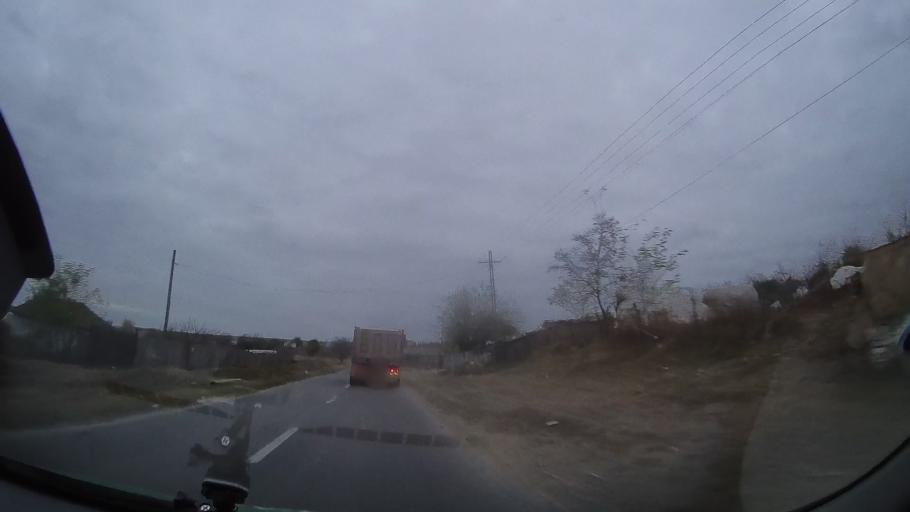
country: RO
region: Tulcea
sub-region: Comuna Mihai Bravu
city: Mihai Bravu
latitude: 44.9562
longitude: 28.6509
